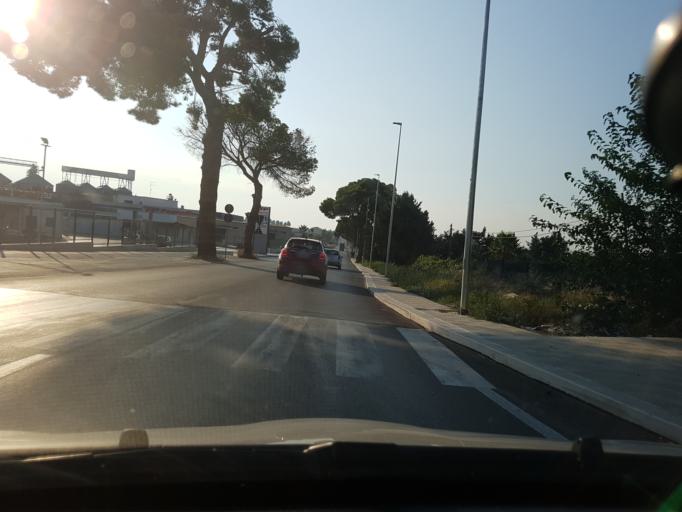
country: IT
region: Apulia
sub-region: Provincia di Foggia
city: Cerignola
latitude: 41.2674
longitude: 15.8851
